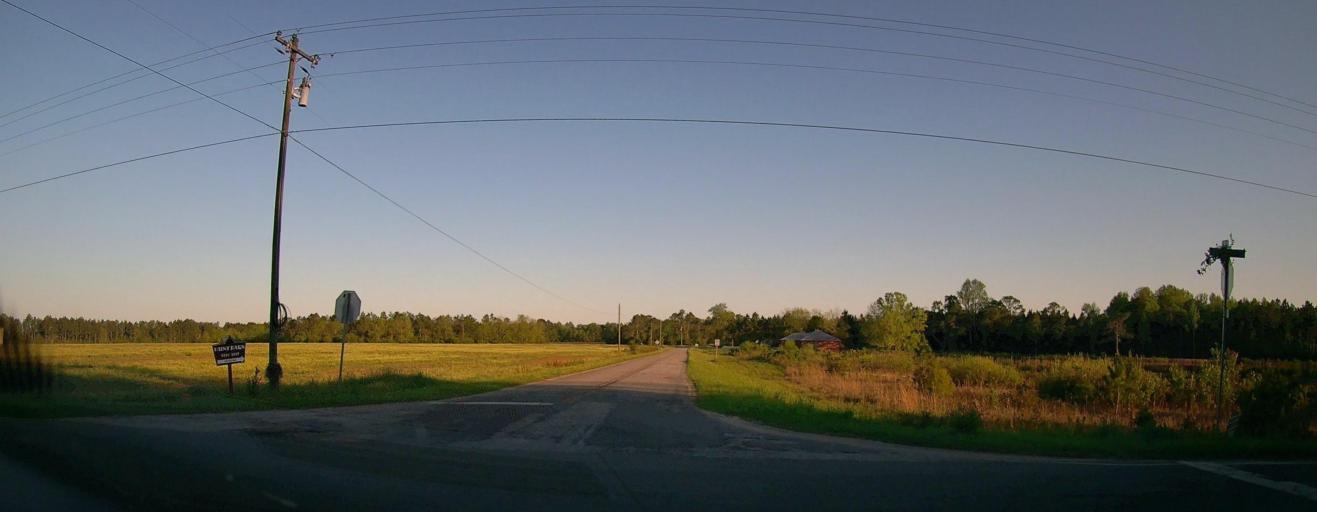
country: US
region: Georgia
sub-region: Ben Hill County
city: Fitzgerald
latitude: 31.6701
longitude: -83.2123
